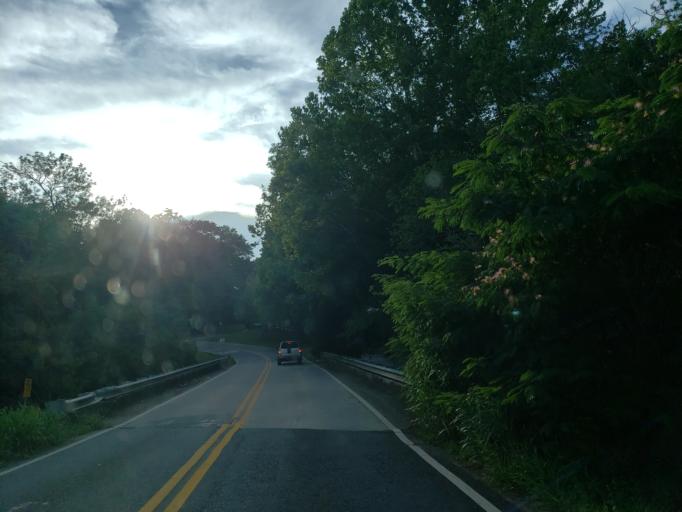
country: US
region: Georgia
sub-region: Bartow County
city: Cartersville
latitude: 34.1985
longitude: -84.8115
